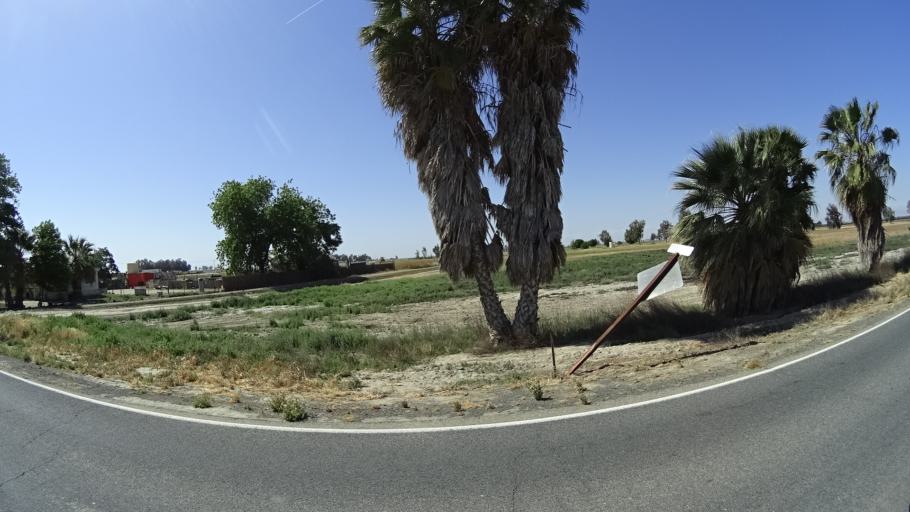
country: US
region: California
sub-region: Kings County
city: Stratford
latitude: 36.2114
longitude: -119.7825
